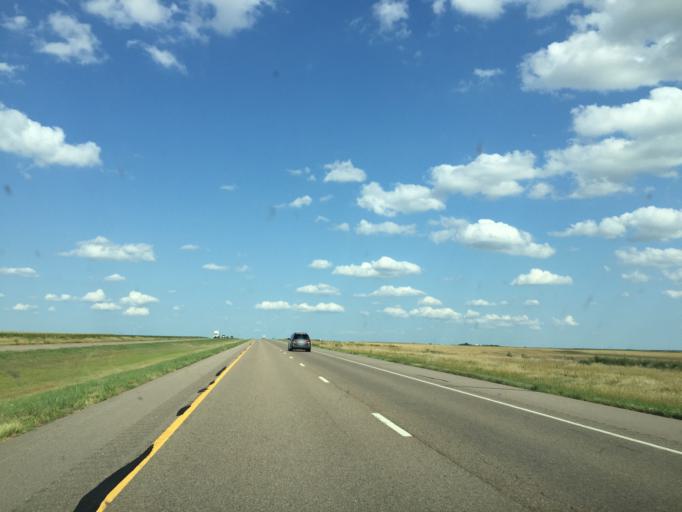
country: US
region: Kansas
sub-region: Trego County
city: WaKeeney
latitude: 39.0238
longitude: -100.1428
